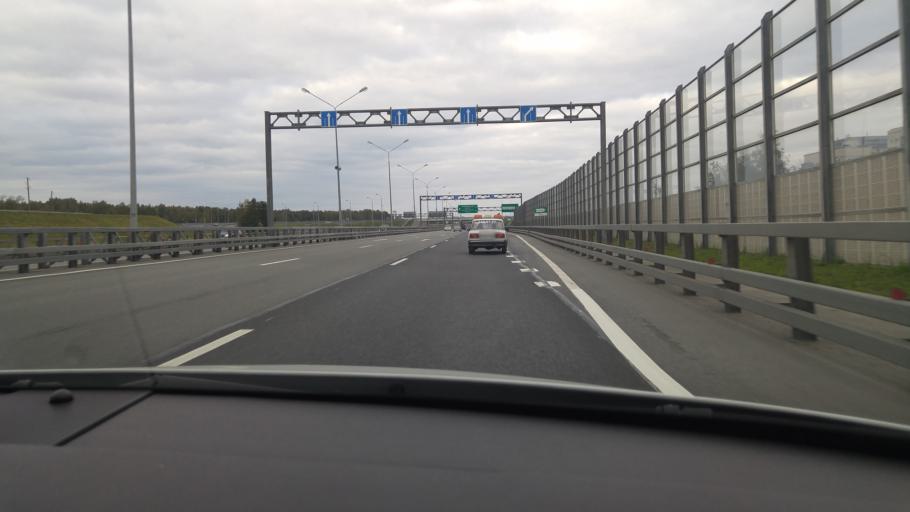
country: RU
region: St.-Petersburg
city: Kronshtadt
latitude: 60.0102
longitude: 29.7147
